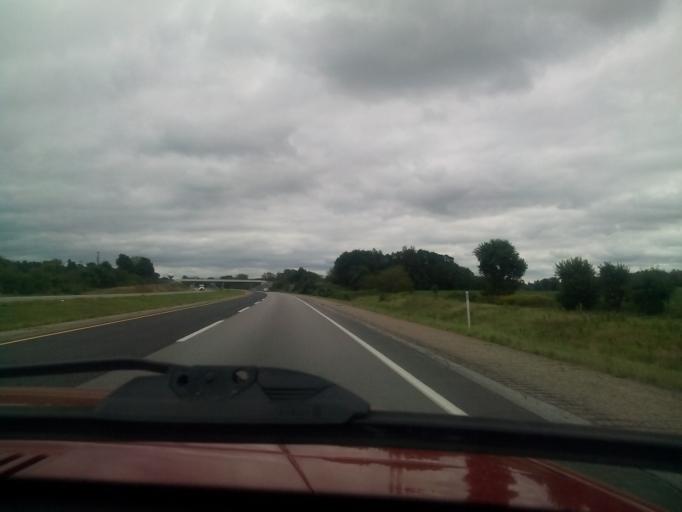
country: US
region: Michigan
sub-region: Berrien County
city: Buchanan
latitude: 41.7339
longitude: -86.3853
